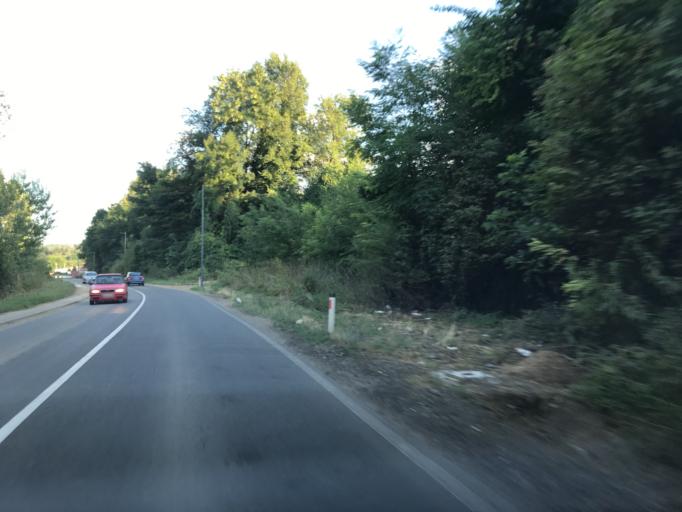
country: RS
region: Central Serbia
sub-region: Belgrade
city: Grocka
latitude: 44.6697
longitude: 20.7232
